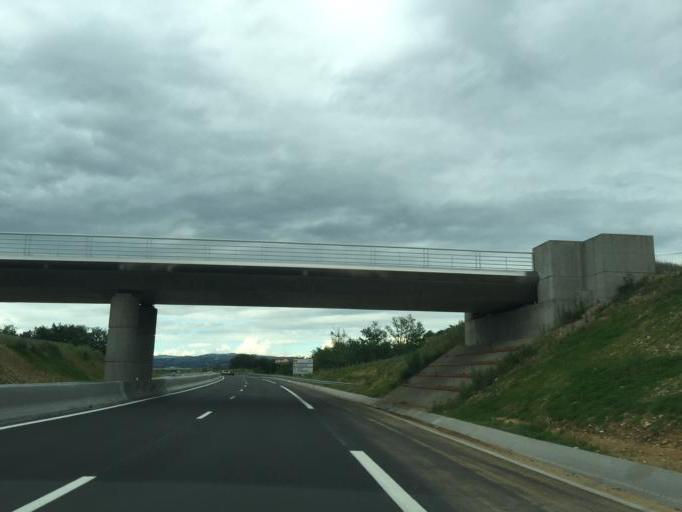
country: FR
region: Rhone-Alpes
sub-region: Departement de la Loire
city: Bonson
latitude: 45.5127
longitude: 4.2157
